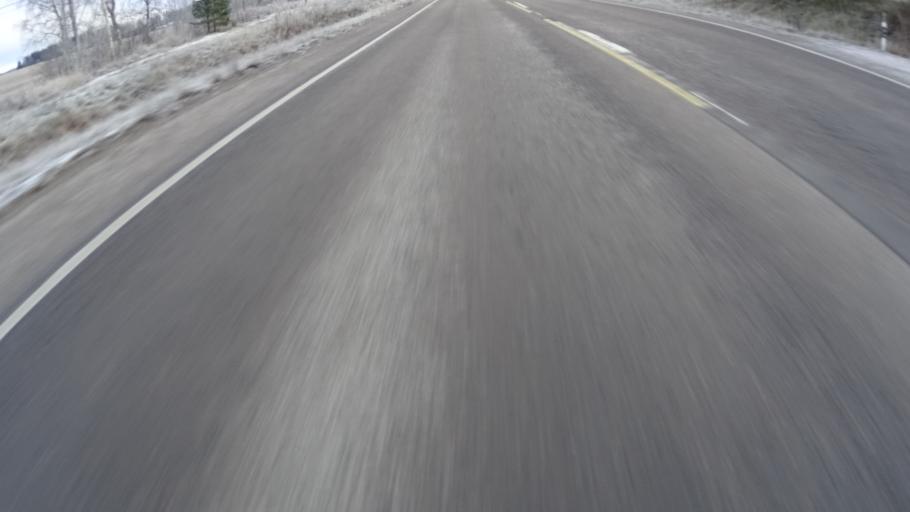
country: FI
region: Uusimaa
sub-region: Helsinki
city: Nurmijaervi
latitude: 60.4333
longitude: 24.7160
